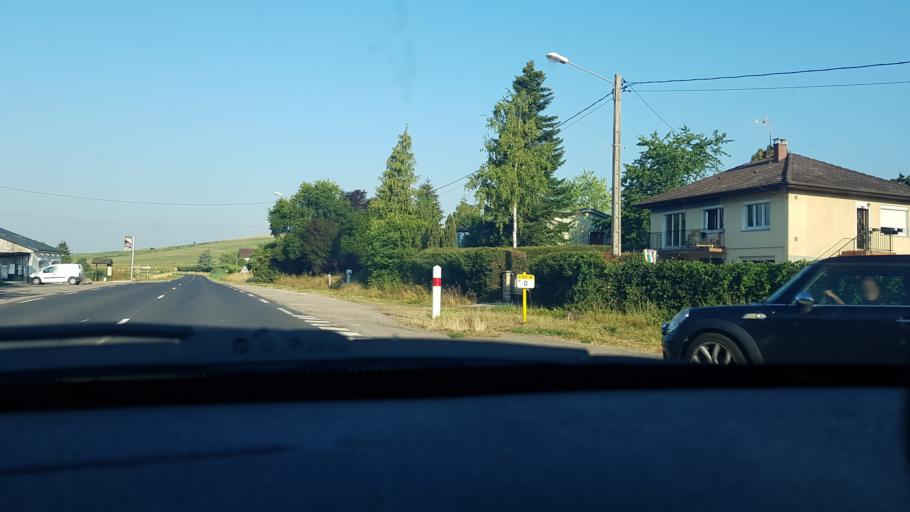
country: FR
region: Lorraine
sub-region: Departement des Vosges
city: Charmes
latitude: 48.3623
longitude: 6.2592
